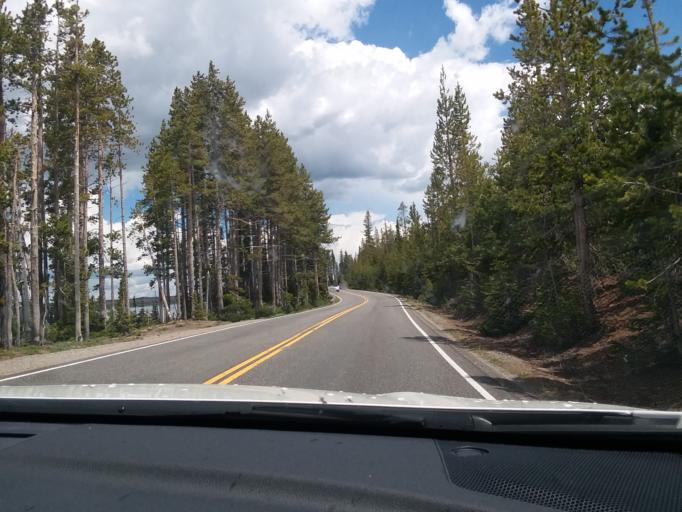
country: US
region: Montana
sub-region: Gallatin County
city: West Yellowstone
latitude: 44.2874
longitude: -110.6261
